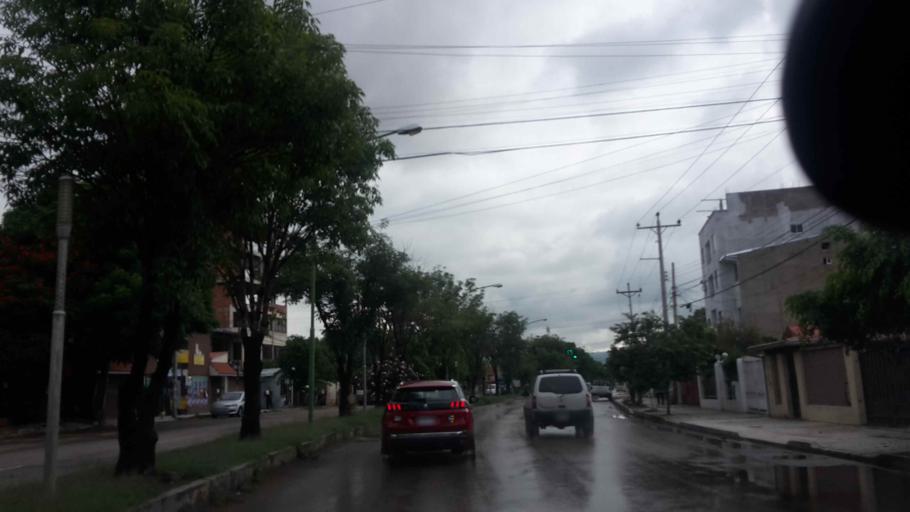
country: BO
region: Cochabamba
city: Cochabamba
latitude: -17.3835
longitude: -66.1768
